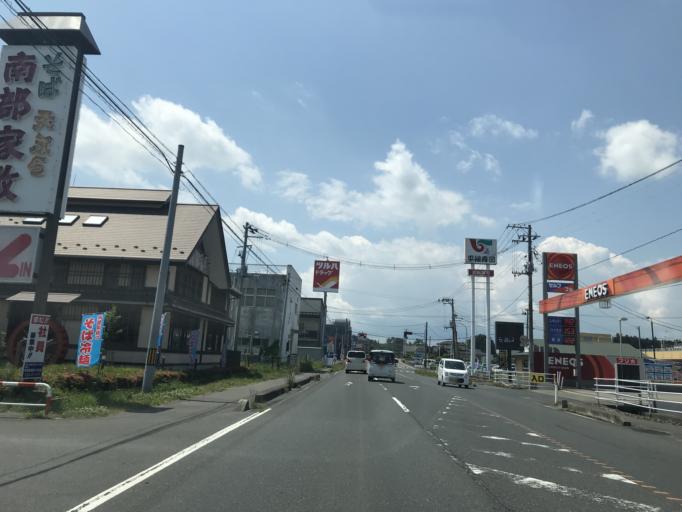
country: JP
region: Miyagi
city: Kogota
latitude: 38.5440
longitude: 141.0599
